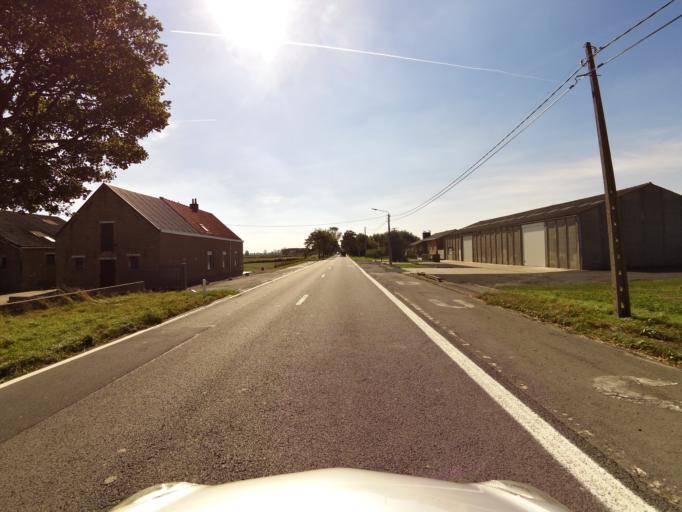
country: BE
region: Flanders
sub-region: Provincie West-Vlaanderen
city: Nieuwpoort
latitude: 51.0891
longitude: 2.8139
